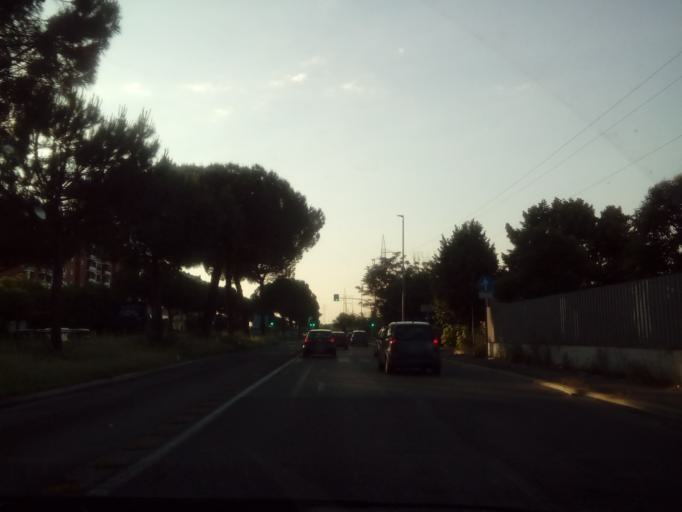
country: IT
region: Latium
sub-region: Citta metropolitana di Roma Capitale
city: Rome
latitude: 41.9155
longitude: 12.5697
